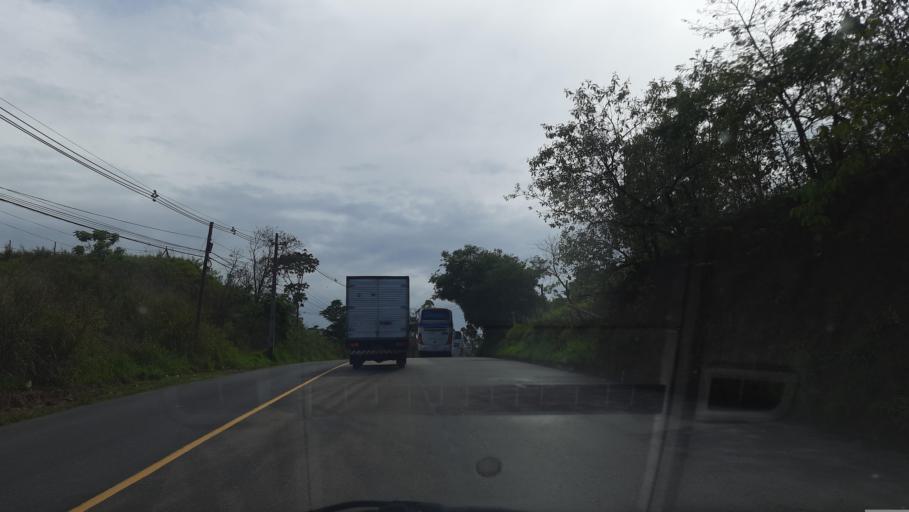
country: BR
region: Sao Paulo
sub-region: Caieiras
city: Caieiras
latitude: -23.3707
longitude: -46.6867
